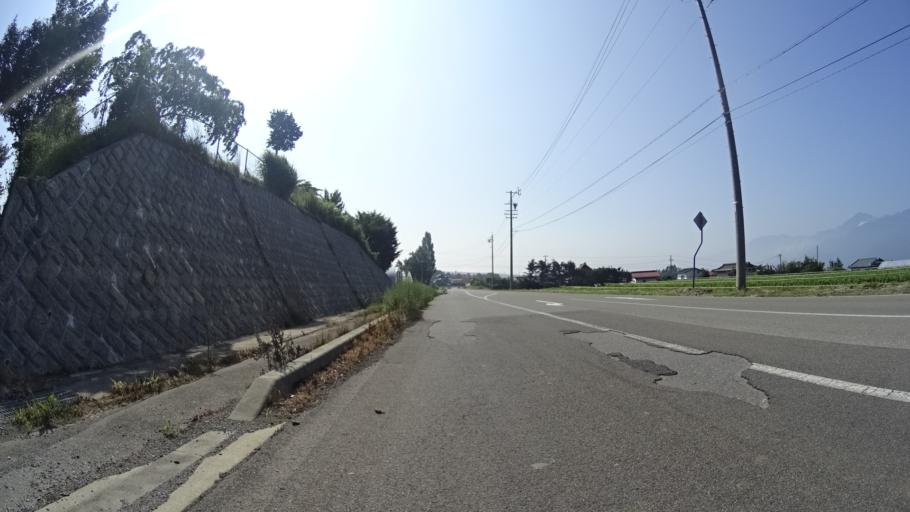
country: JP
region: Nagano
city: Chino
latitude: 35.9369
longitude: 138.2588
